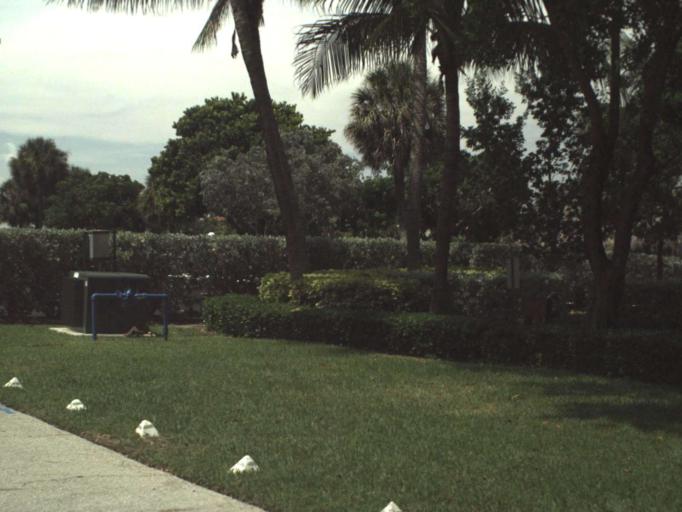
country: US
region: Florida
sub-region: Broward County
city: Lighthouse Point
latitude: 26.2812
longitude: -80.0798
